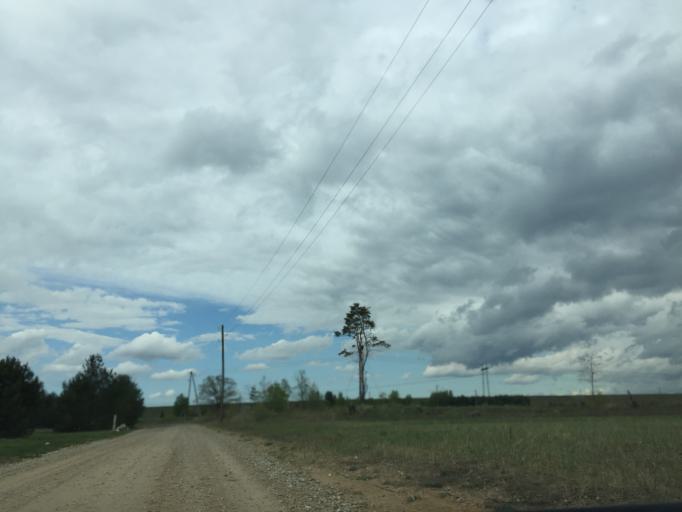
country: LV
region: Kekava
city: Kekava
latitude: 56.8161
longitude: 24.2939
